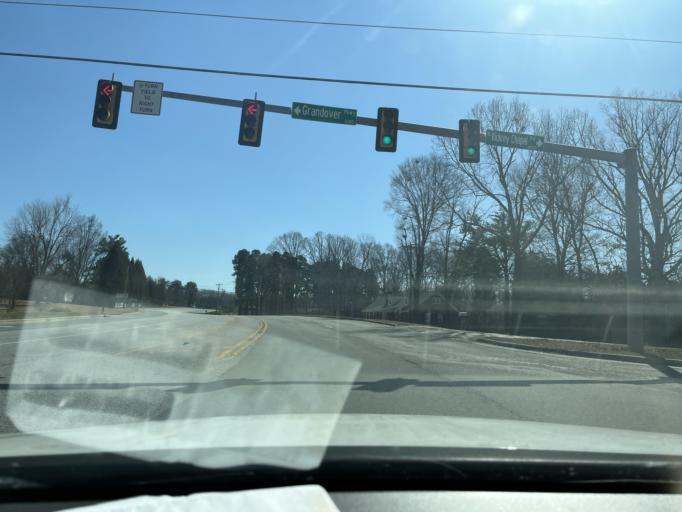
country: US
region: North Carolina
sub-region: Guilford County
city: Jamestown
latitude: 35.9864
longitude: -79.9032
